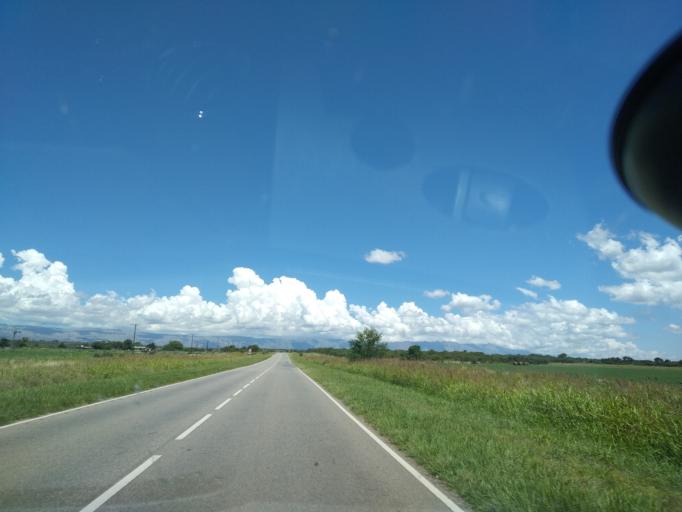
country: AR
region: Cordoba
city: Villa Cura Brochero
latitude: -31.6744
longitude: -65.0902
